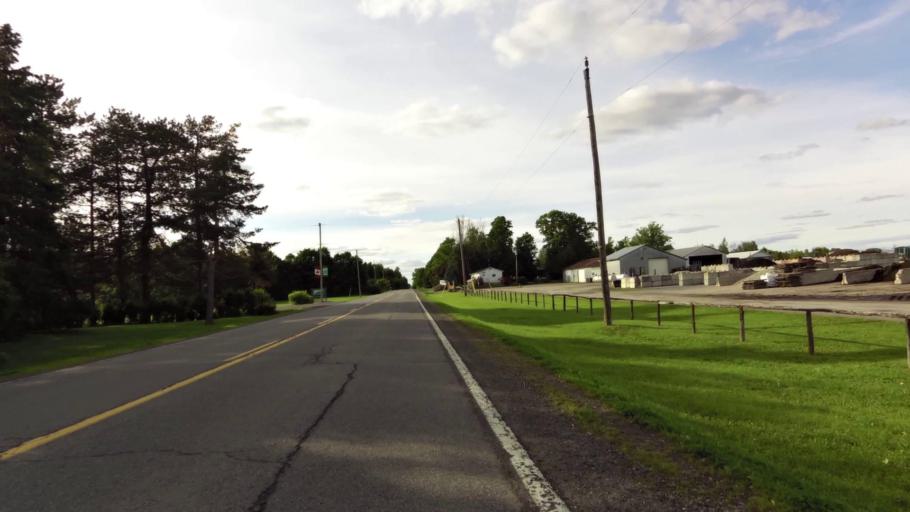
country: CA
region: Ontario
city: Ottawa
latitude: 45.1971
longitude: -75.5896
